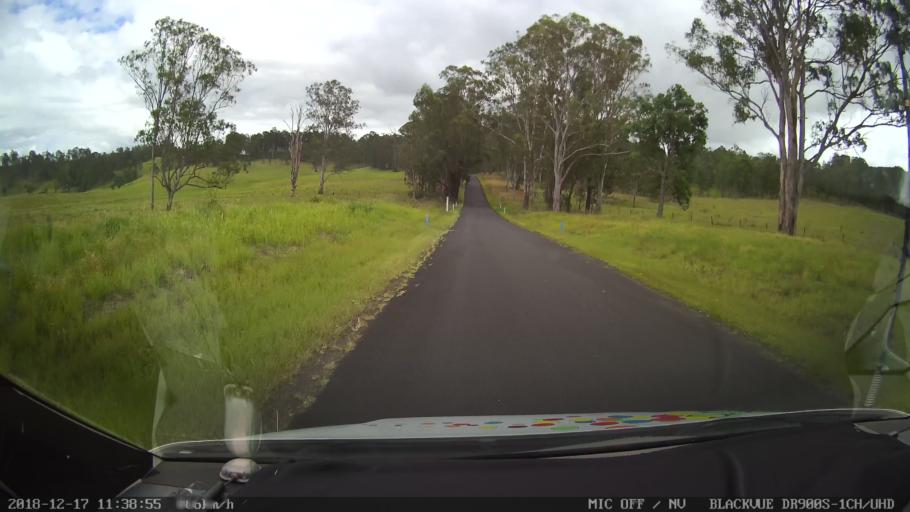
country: AU
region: New South Wales
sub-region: Kyogle
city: Kyogle
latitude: -28.6915
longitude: 152.5971
